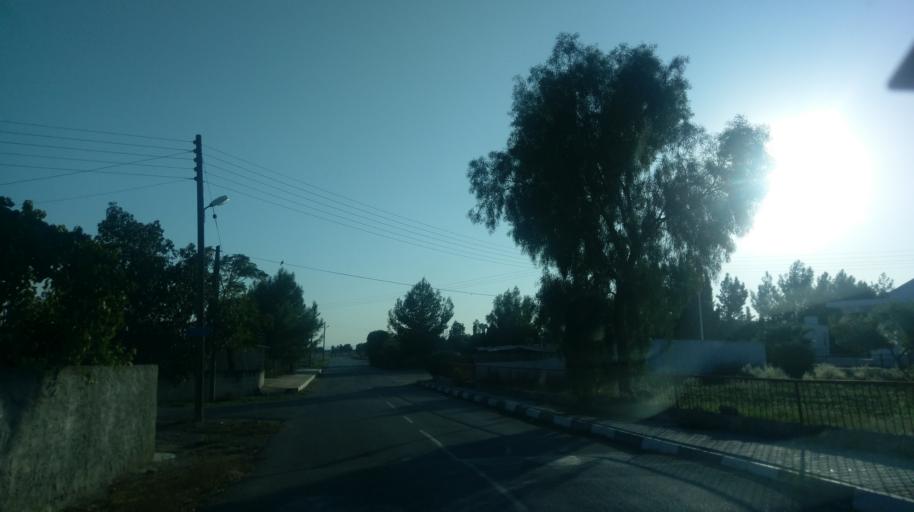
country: CY
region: Ammochostos
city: Lefkonoiko
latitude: 35.2443
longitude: 33.6480
